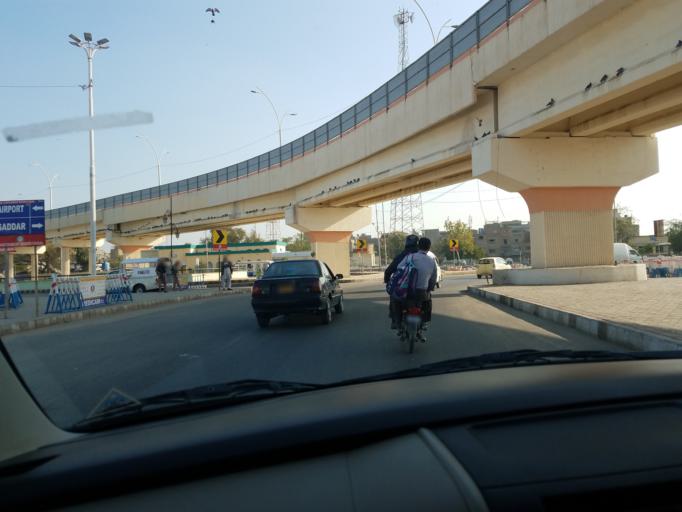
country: PK
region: Sindh
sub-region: Karachi District
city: Karachi
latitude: 24.8875
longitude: 67.1252
